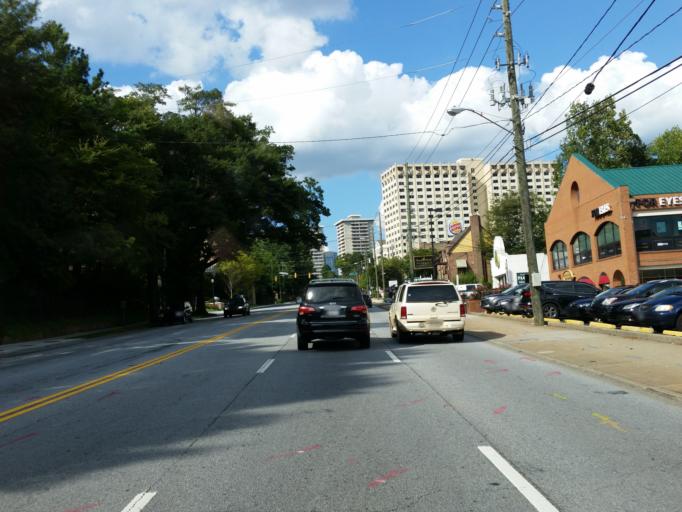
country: US
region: Georgia
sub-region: DeKalb County
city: Druid Hills
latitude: 33.8198
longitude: -84.3885
